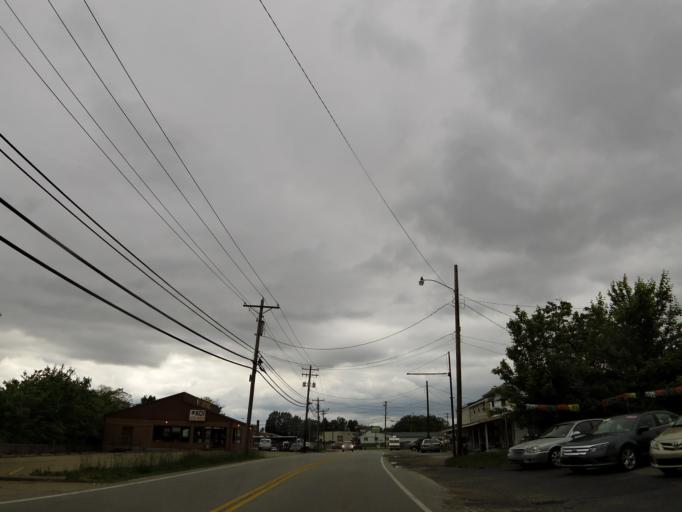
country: US
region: Kentucky
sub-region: Grant County
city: Williamstown
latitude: 38.6500
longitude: -84.5680
